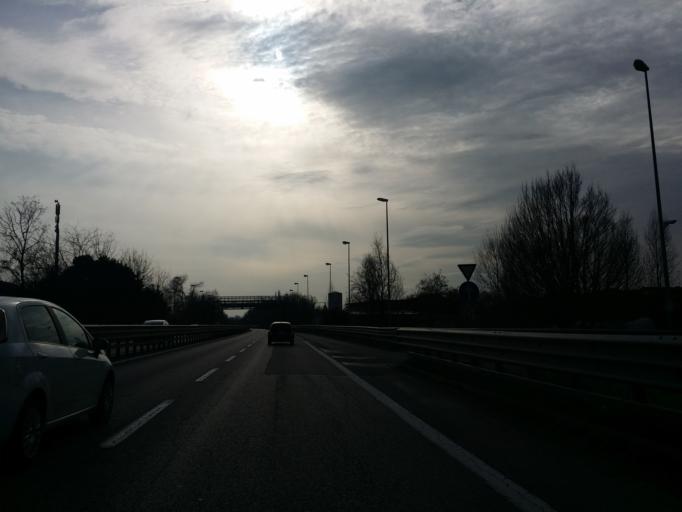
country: IT
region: Veneto
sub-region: Provincia di Padova
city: Caselle
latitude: 45.4051
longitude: 11.8488
